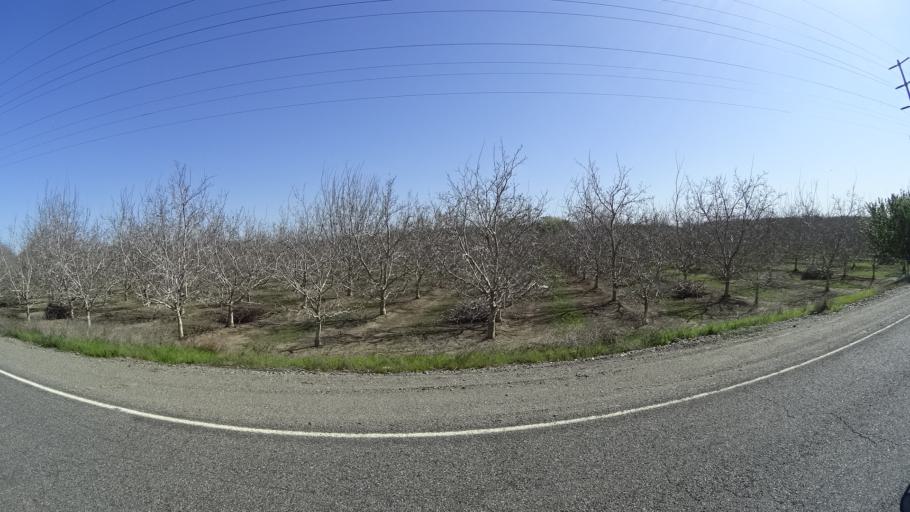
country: US
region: California
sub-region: Glenn County
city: Hamilton City
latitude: 39.7721
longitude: -122.0357
